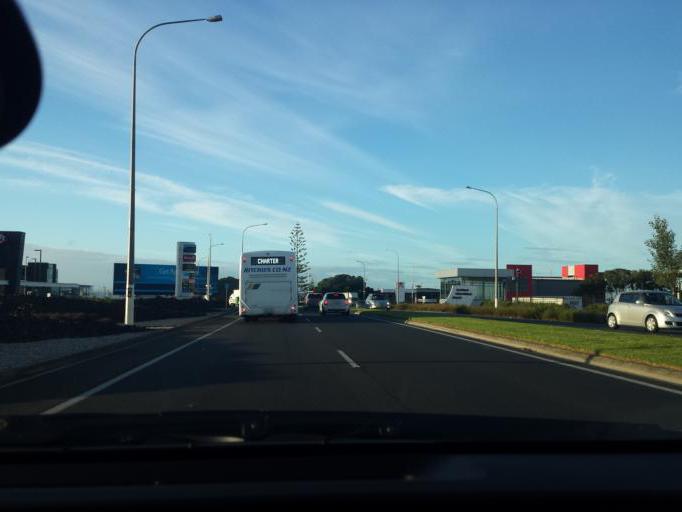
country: NZ
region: Auckland
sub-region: Auckland
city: Mangere
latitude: -36.9973
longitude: 174.7869
